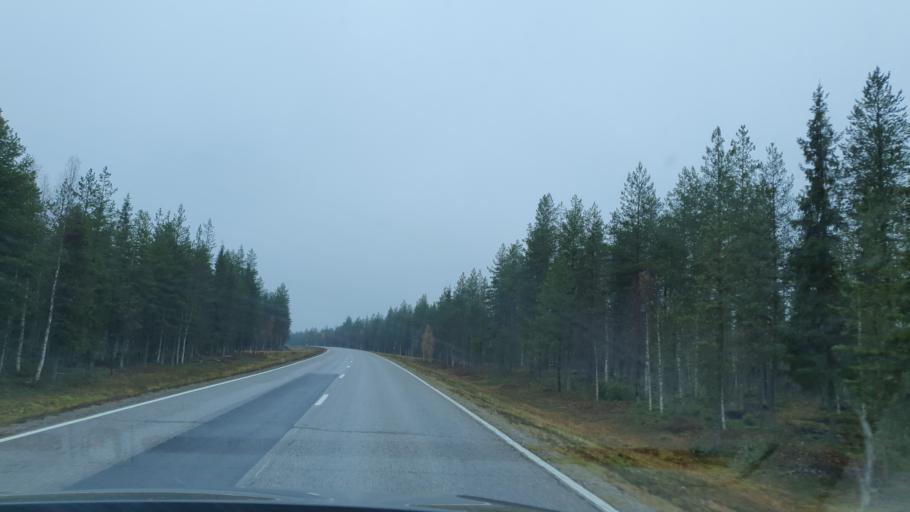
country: FI
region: Lapland
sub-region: Tunturi-Lappi
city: Kittilae
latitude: 67.3713
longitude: 24.8911
